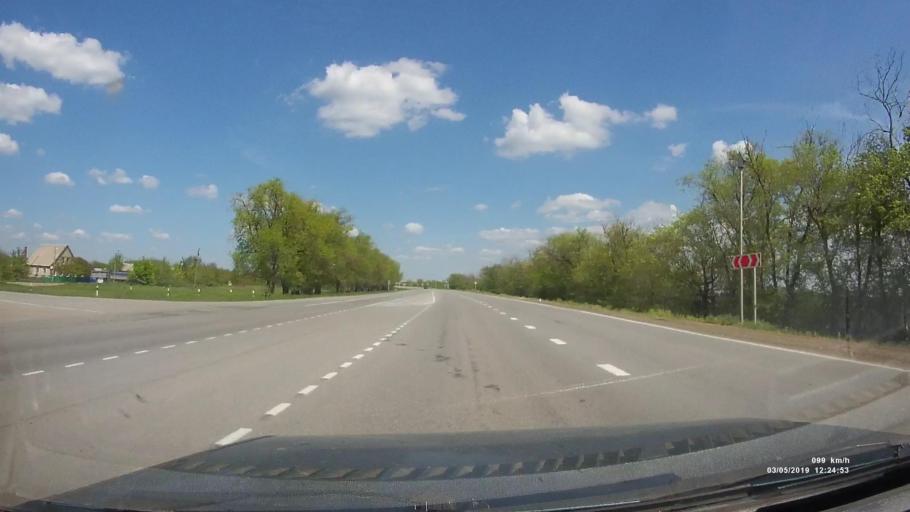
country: RU
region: Rostov
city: Semikarakorsk
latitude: 47.4252
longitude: 40.7061
